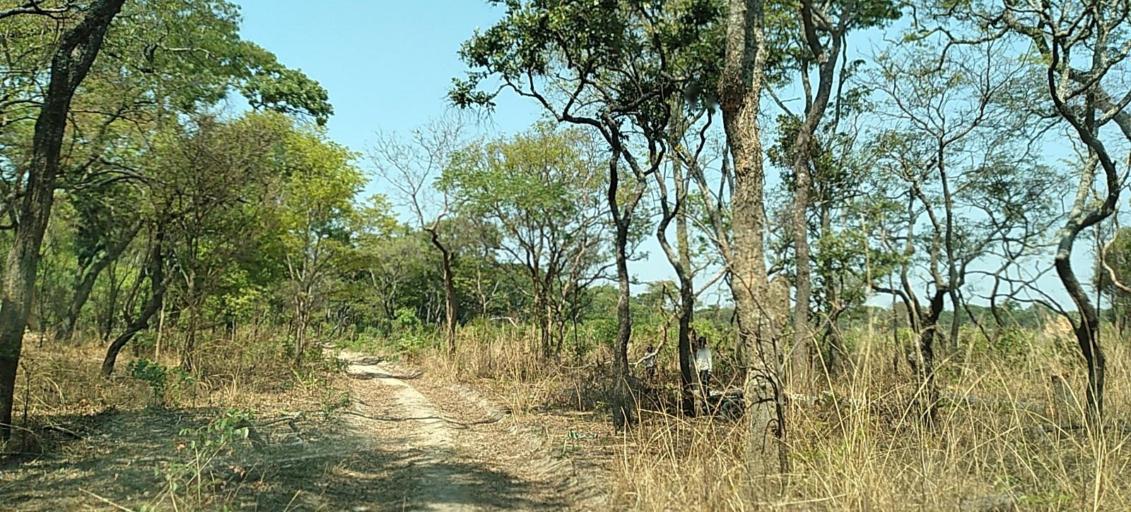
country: ZM
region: Copperbelt
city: Mpongwe
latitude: -13.7948
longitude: 28.0862
